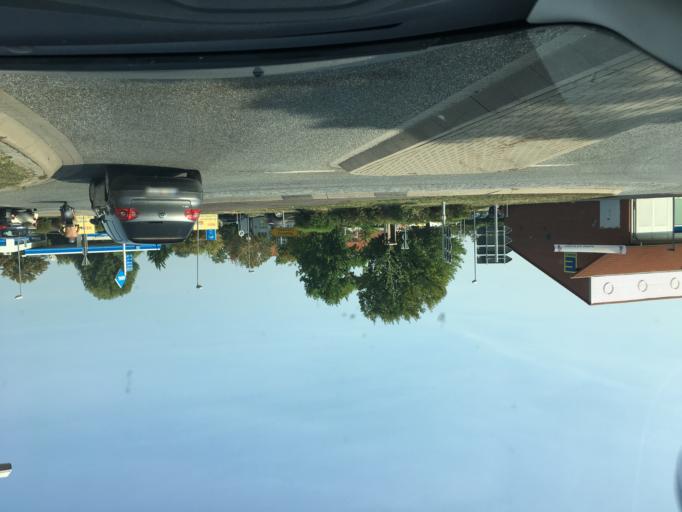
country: DE
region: Saxony-Anhalt
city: Calbe
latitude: 51.9117
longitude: 11.7773
